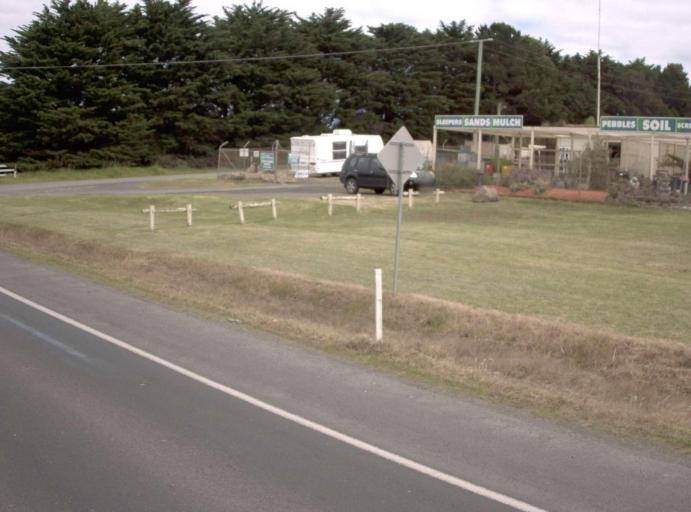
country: AU
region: Victoria
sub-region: Bass Coast
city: Phillip Island
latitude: -38.5147
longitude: 145.3511
